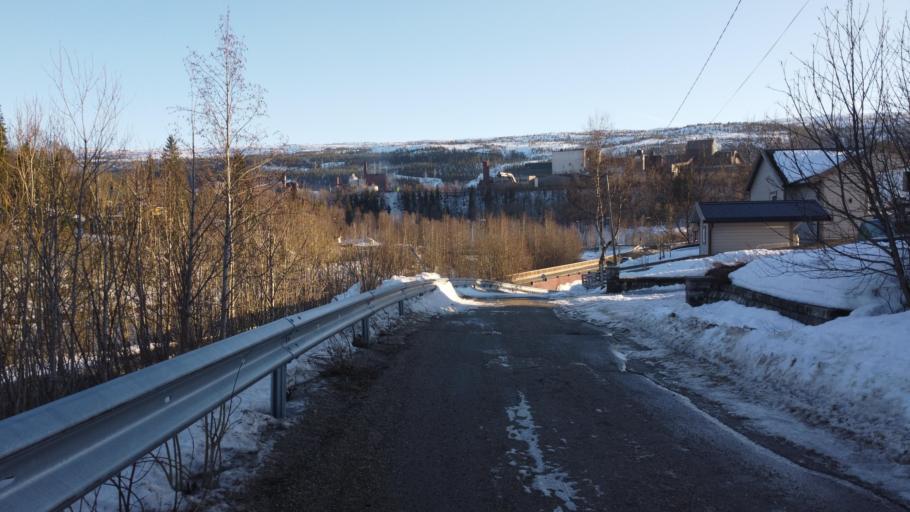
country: NO
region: Nordland
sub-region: Rana
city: Mo i Rana
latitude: 66.3183
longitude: 14.1686
